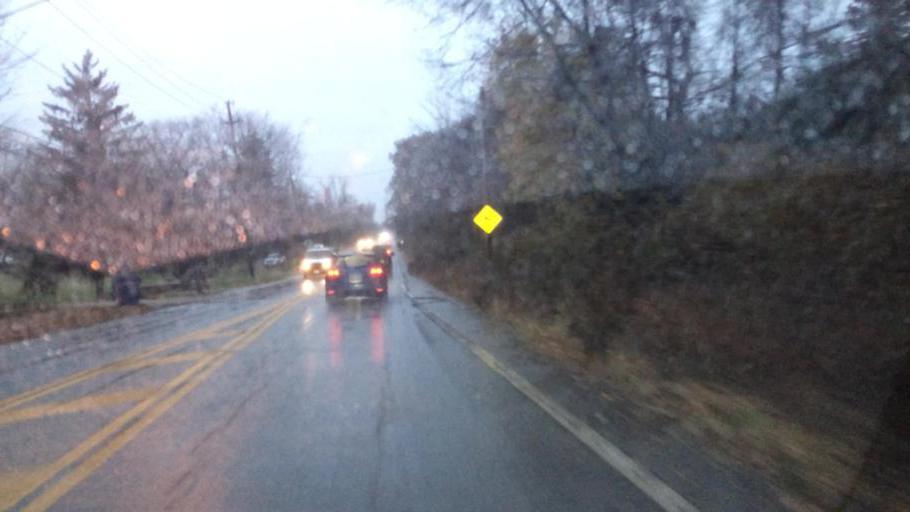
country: US
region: Ohio
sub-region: Cuyahoga County
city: Olmsted Falls
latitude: 41.3921
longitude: -81.9030
